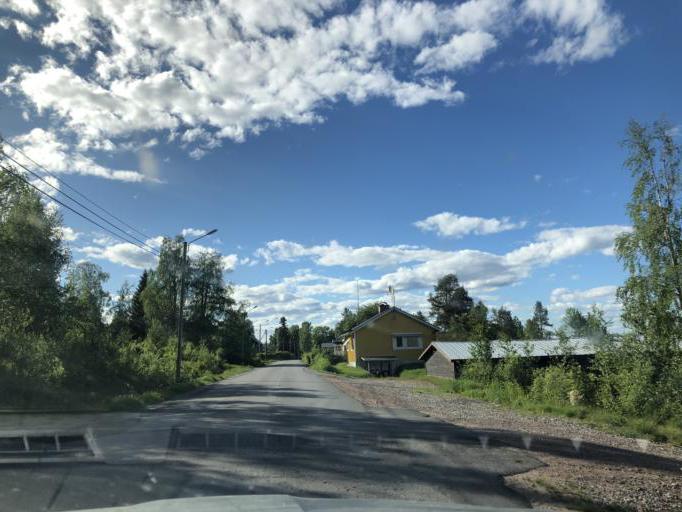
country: SE
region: Norrbotten
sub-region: Overkalix Kommun
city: OEverkalix
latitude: 66.3201
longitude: 22.8641
